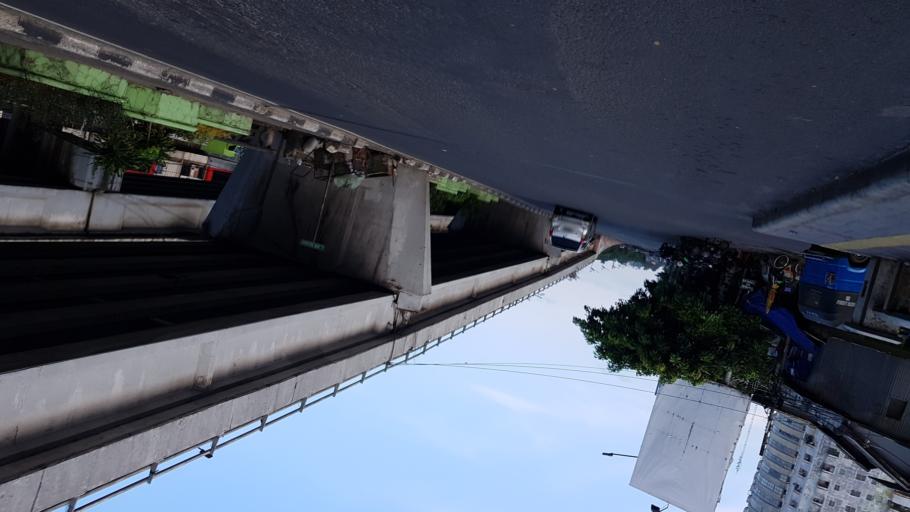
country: ID
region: Jakarta Raya
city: Jakarta
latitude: -6.1428
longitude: 106.7932
